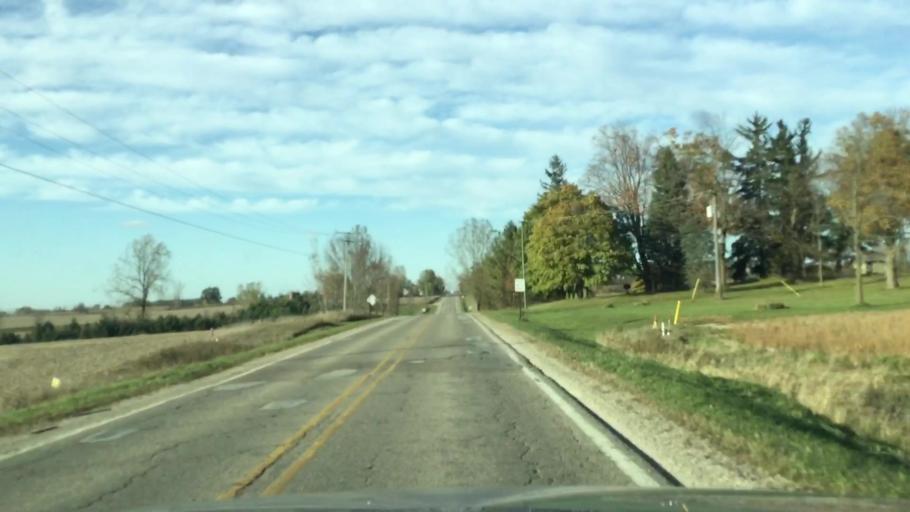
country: US
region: Michigan
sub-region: Lapeer County
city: North Branch
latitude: 43.2419
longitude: -83.1974
